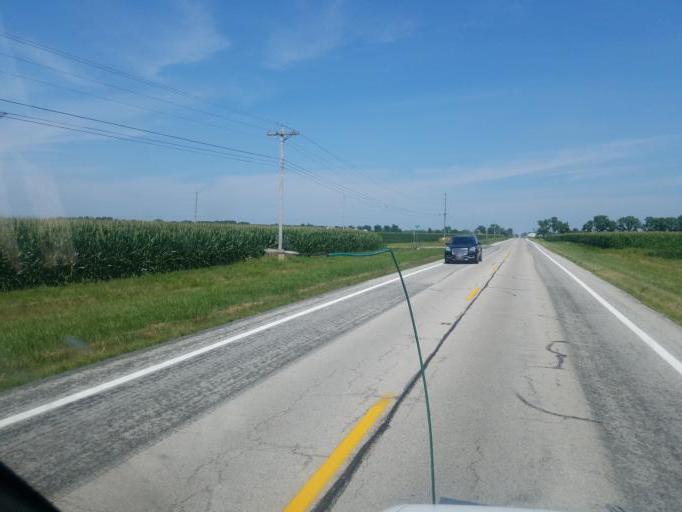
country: US
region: Ohio
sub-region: Auglaize County
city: Saint Marys
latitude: 40.4949
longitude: -84.4450
